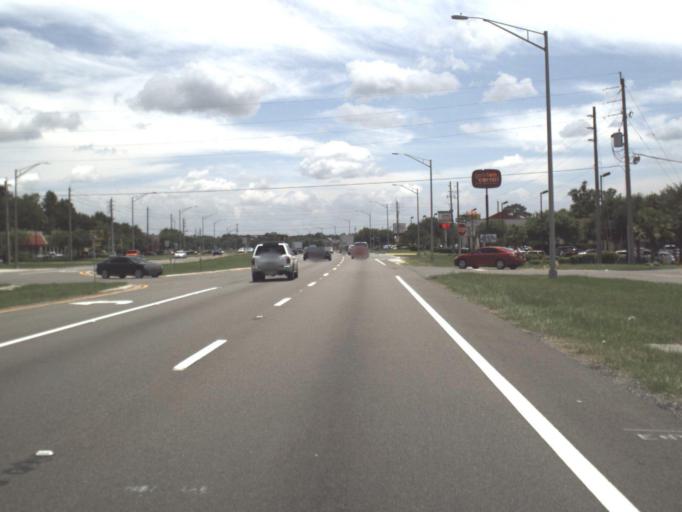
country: US
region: Florida
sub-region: Duval County
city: Jacksonville
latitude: 30.2725
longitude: -81.5592
